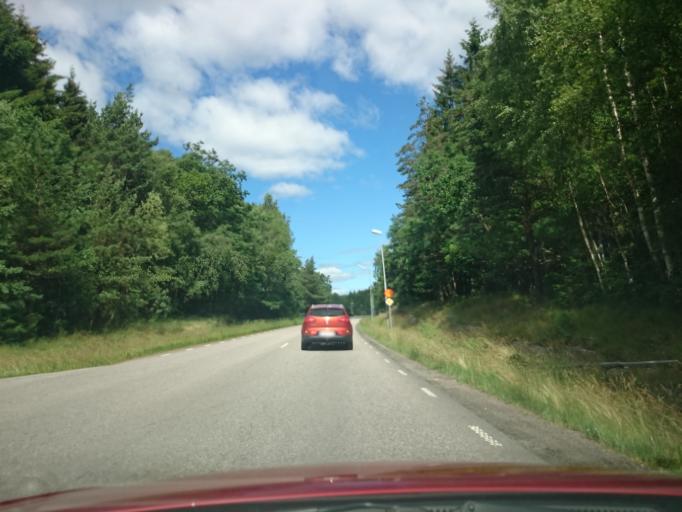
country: SE
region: Vaestra Goetaland
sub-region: Lerums Kommun
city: Grabo
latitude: 57.8256
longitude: 12.2925
